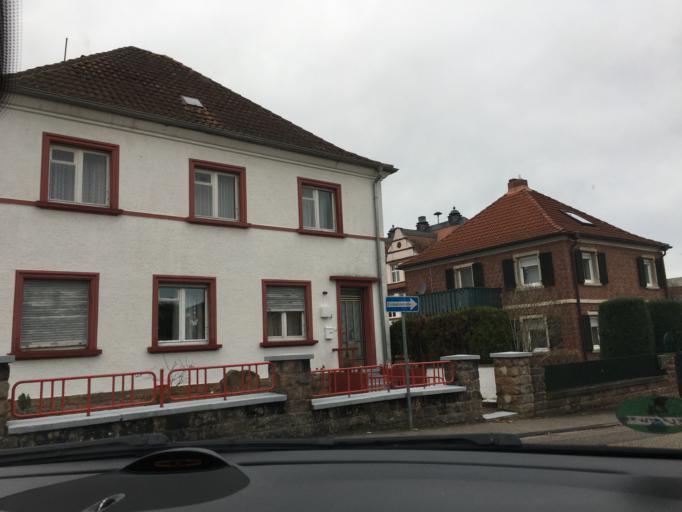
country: DE
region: Rheinland-Pfalz
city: Waldfischbach-Burgalben
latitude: 49.2851
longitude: 7.6517
